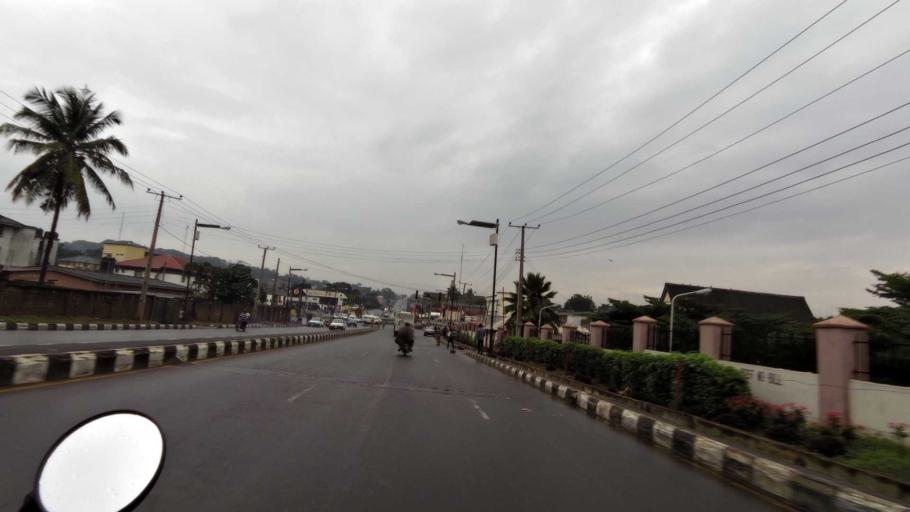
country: NG
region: Oyo
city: Ibadan
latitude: 7.3985
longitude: 3.9079
